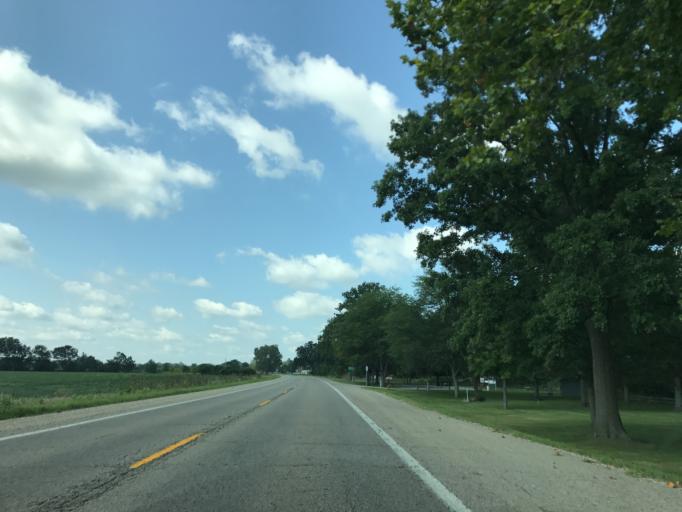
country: US
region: Michigan
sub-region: Branch County
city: Bronson
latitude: 41.8647
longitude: -85.2255
